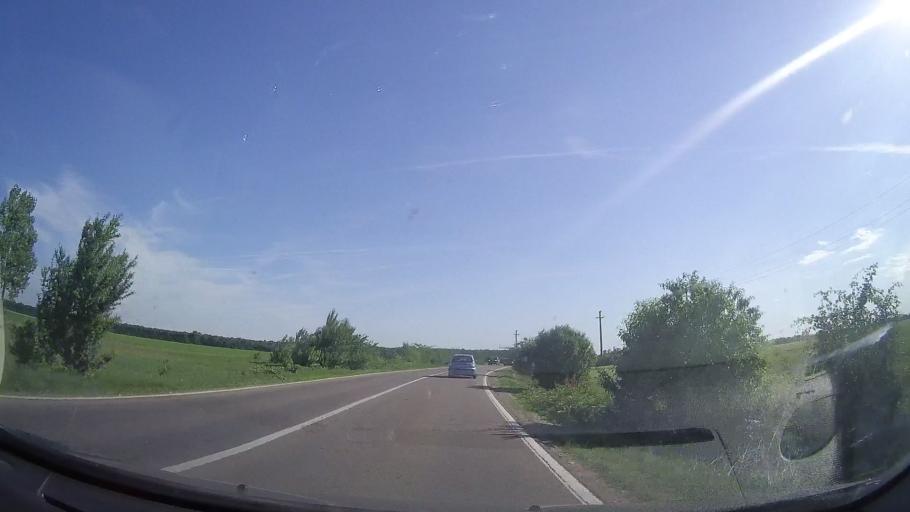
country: RO
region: Prahova
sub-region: Comuna Berceni
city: Corlatesti
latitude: 44.9197
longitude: 26.1015
